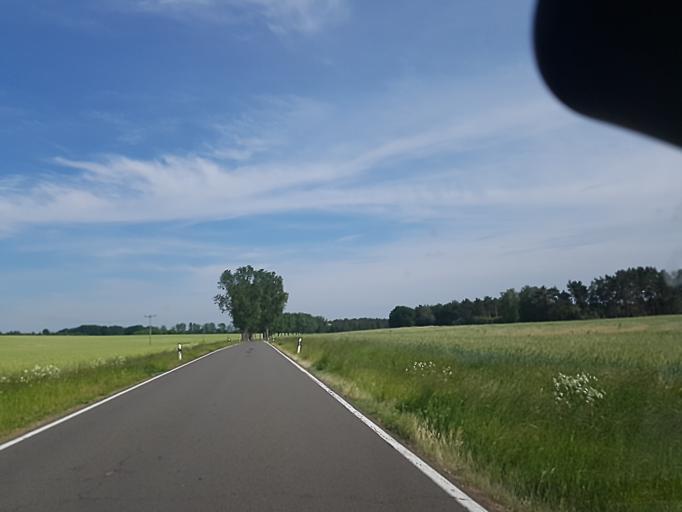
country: DE
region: Saxony-Anhalt
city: Kropstadt
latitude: 51.9744
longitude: 12.7286
